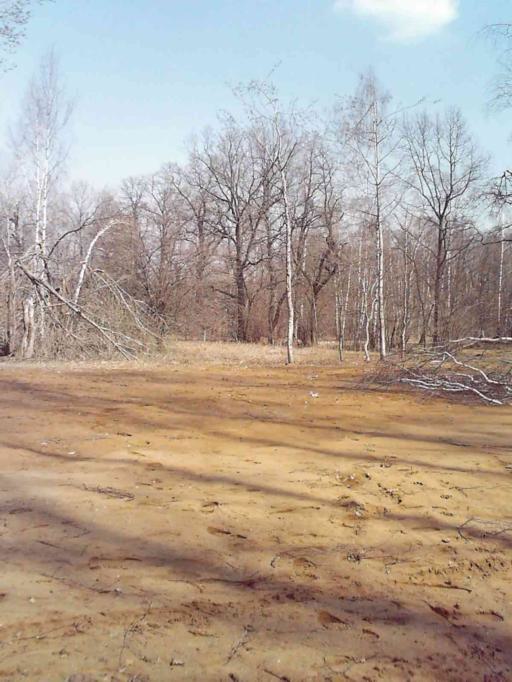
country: RU
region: Moscow
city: Yasenevo
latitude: 55.5795
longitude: 37.5378
